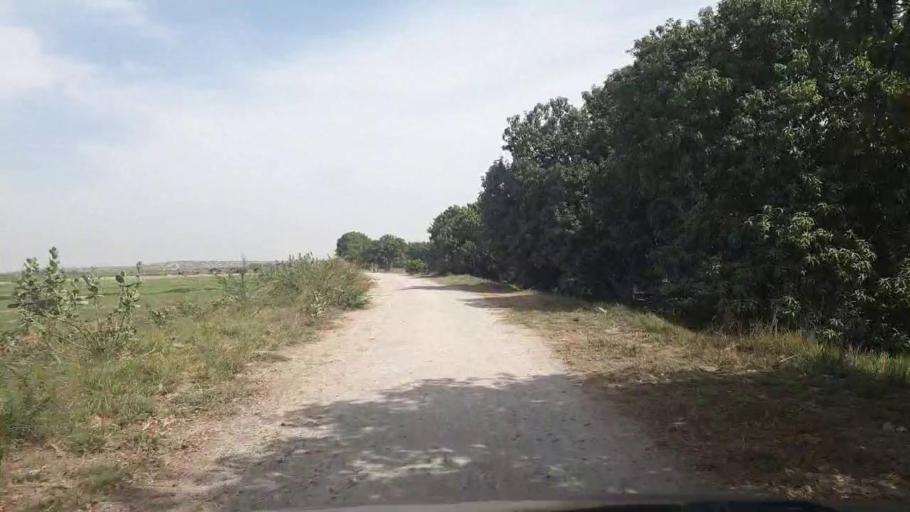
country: PK
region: Sindh
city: Kunri
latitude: 25.2087
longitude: 69.6935
